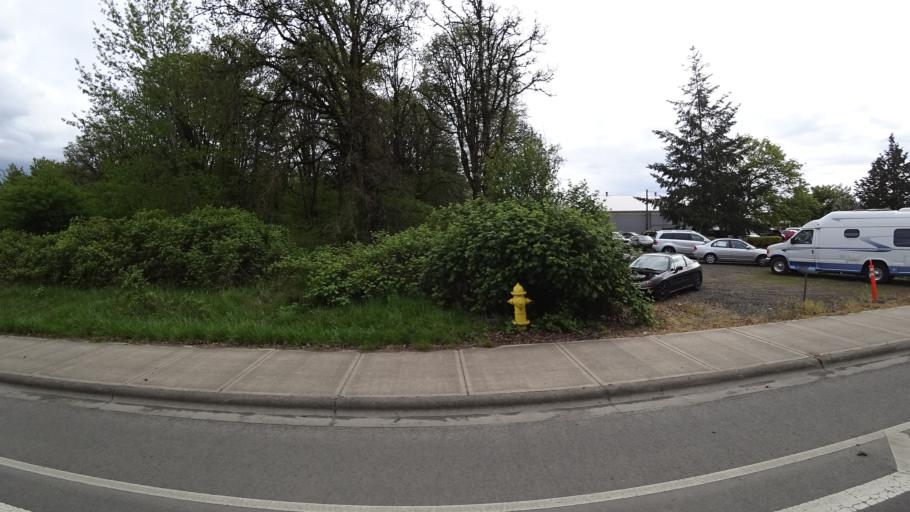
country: US
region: Oregon
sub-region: Washington County
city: Hillsboro
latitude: 45.5510
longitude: -122.9442
